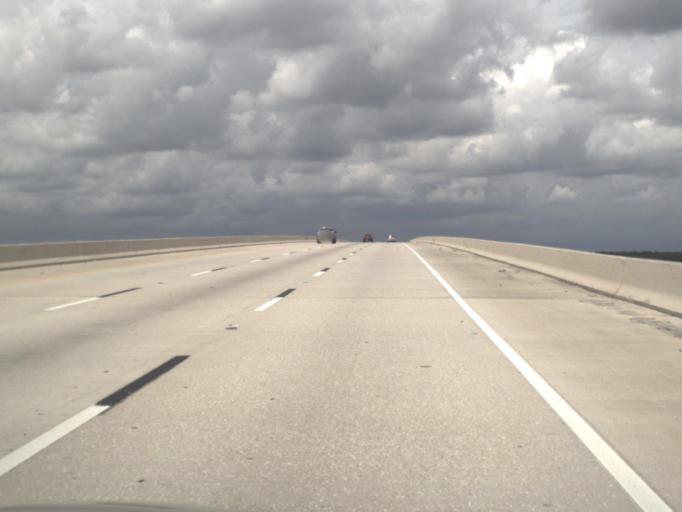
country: US
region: Florida
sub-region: Charlotte County
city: Cleveland
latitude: 26.9567
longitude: -82.0202
